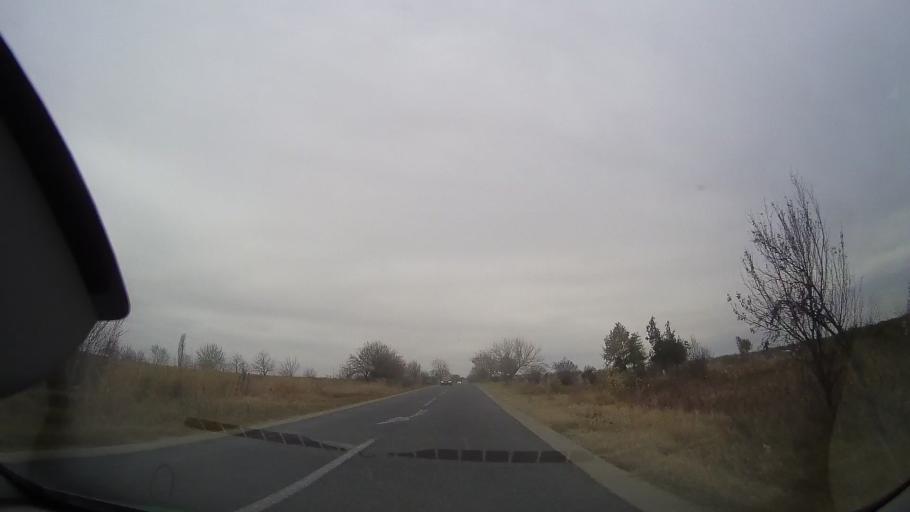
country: RO
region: Braila
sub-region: Comuna Ciocile
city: Ciocile
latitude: 44.7752
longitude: 27.1736
